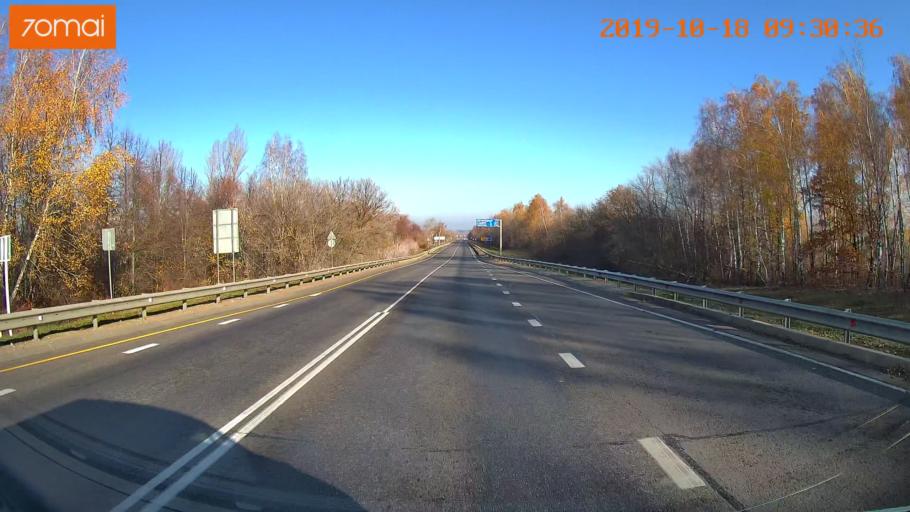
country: RU
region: Tula
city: Yefremov
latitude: 53.1402
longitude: 38.1596
